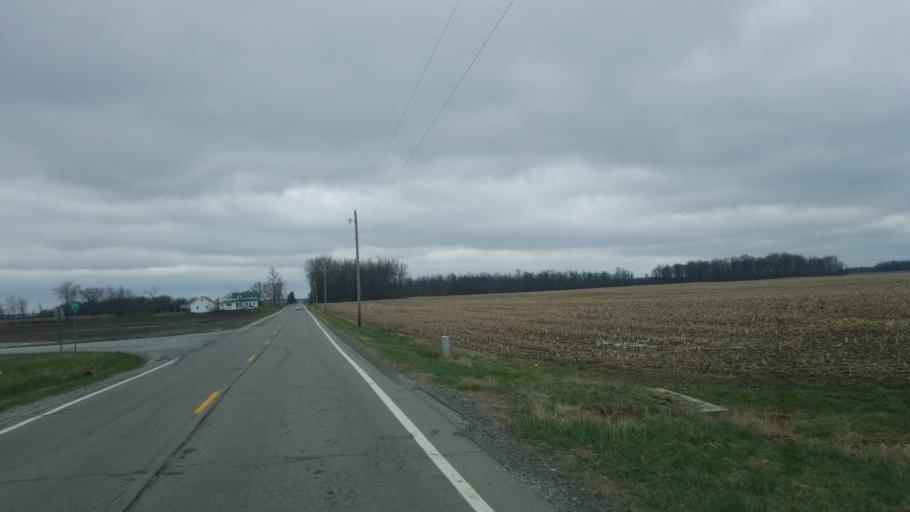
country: US
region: Ohio
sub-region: Hardin County
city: Kenton
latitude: 40.7002
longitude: -83.5761
